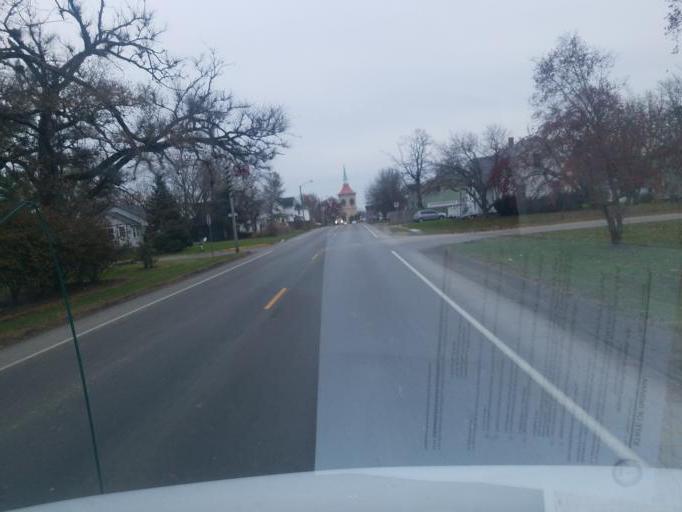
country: US
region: Indiana
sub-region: Adams County
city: Berne
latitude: 40.6617
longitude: -84.9556
